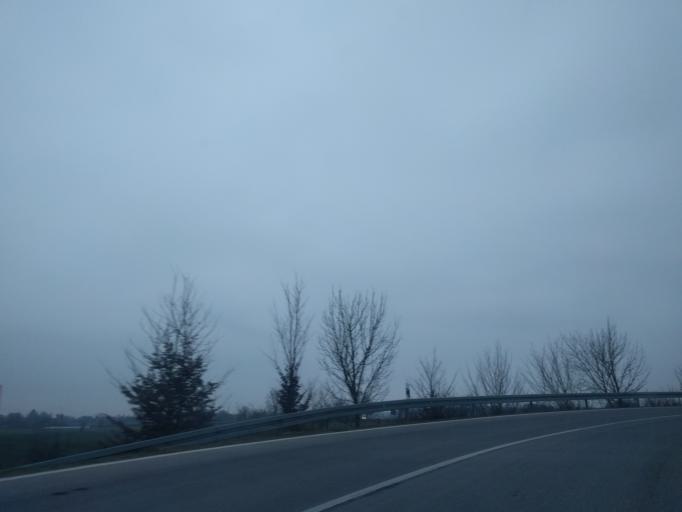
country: DE
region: Bavaria
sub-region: Swabia
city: Donauwoerth
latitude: 48.7041
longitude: 10.7856
